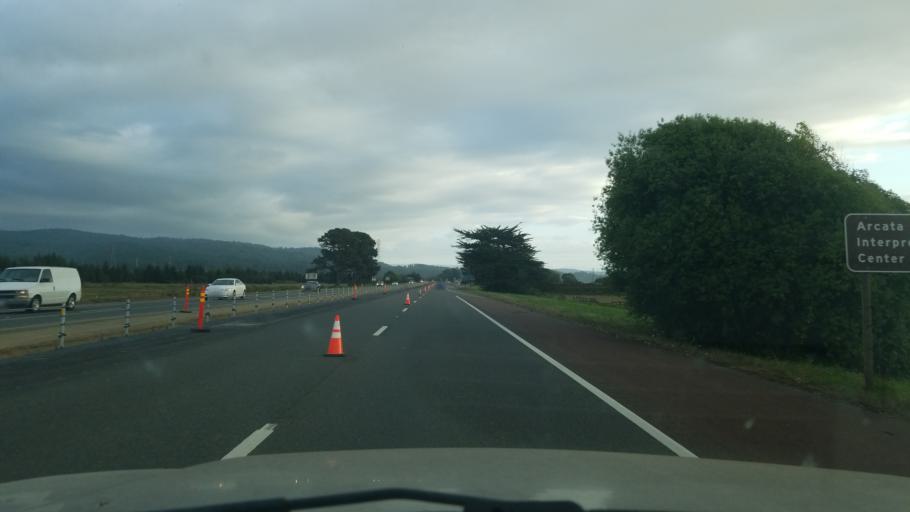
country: US
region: California
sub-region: Humboldt County
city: Arcata
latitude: 40.8557
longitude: -124.0823
